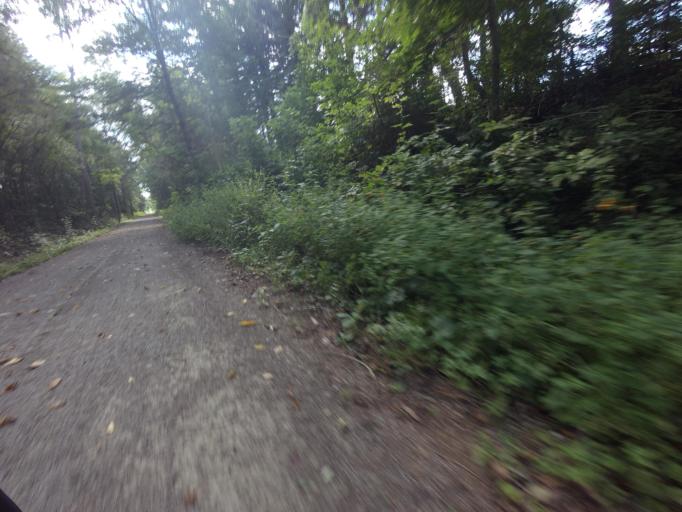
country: CA
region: Ontario
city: Huron East
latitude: 43.7241
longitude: -81.4063
